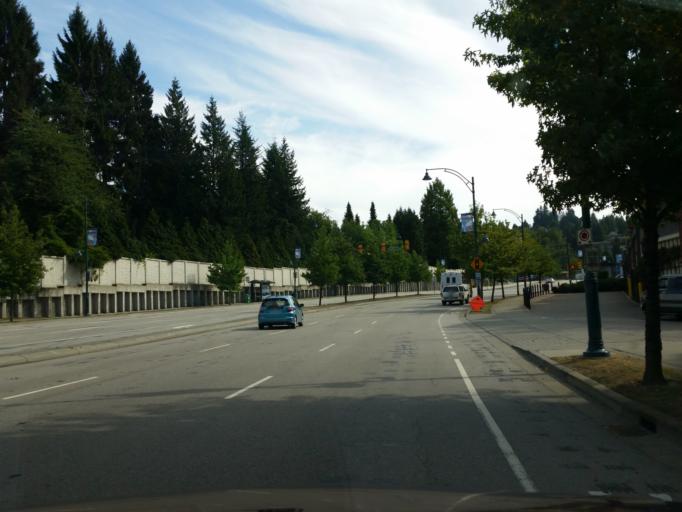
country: CA
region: British Columbia
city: Port Moody
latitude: 49.2804
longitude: -122.8275
